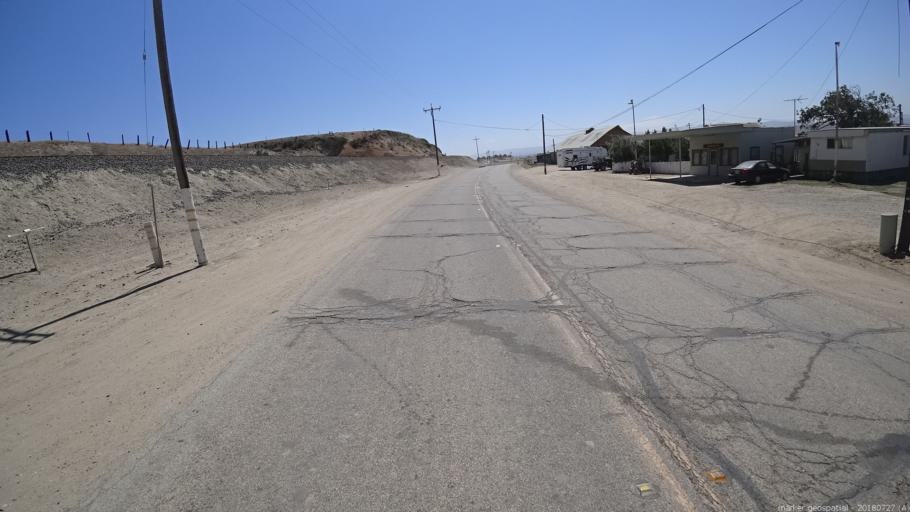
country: US
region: California
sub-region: Monterey County
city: King City
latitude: 36.1805
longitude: -121.0608
